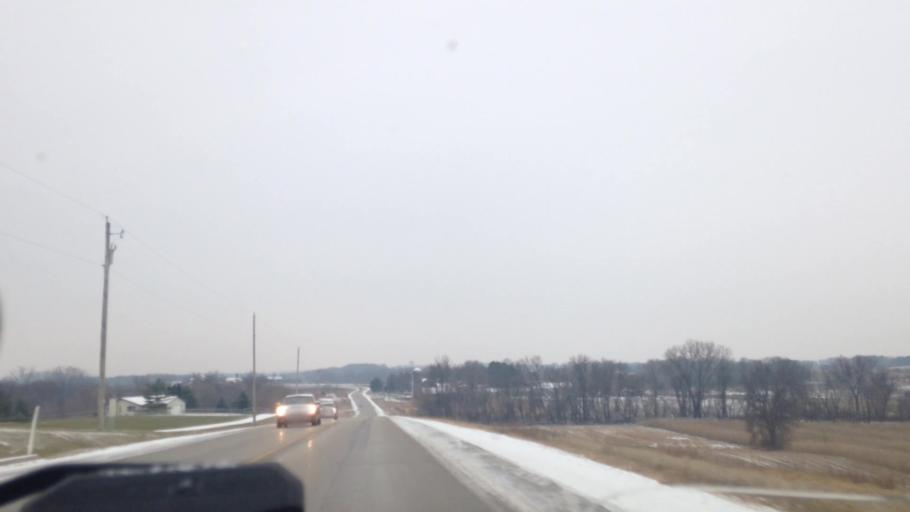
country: US
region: Wisconsin
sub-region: Dodge County
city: Hustisford
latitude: 43.3821
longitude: -88.5419
